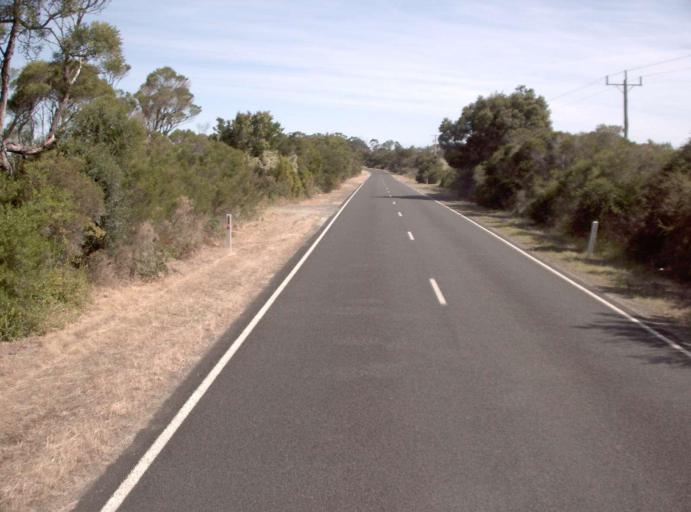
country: AU
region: Victoria
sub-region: Wellington
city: Sale
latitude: -38.3501
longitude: 147.1718
